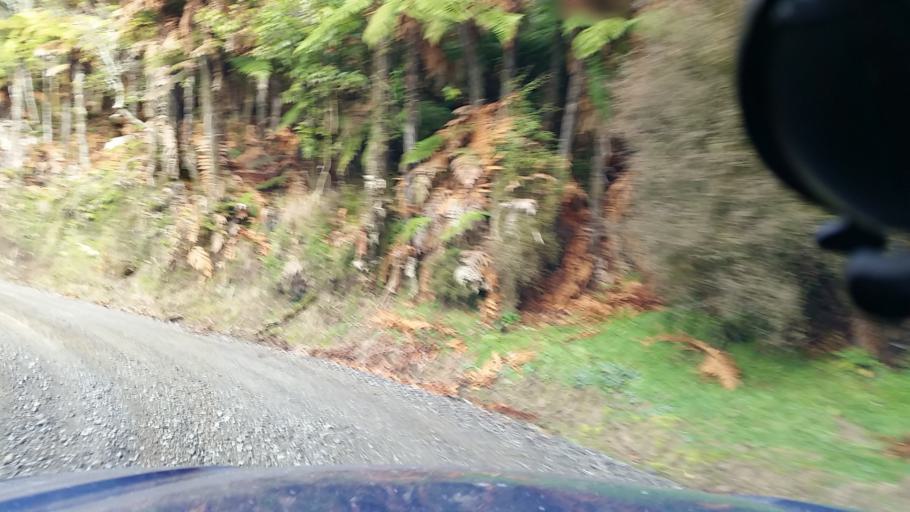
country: NZ
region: Taranaki
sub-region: New Plymouth District
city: Waitara
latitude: -39.0021
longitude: 174.7646
